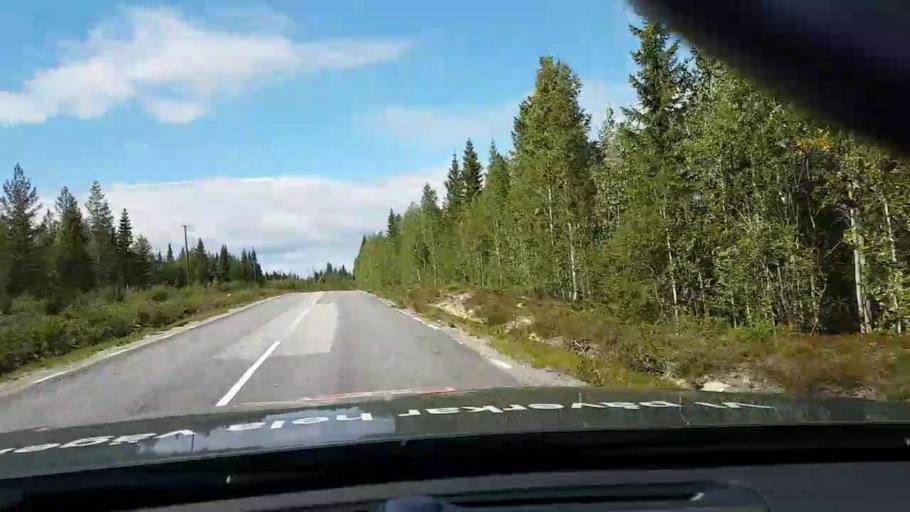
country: SE
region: Vaesterbotten
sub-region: Asele Kommun
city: Asele
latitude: 63.8199
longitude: 17.4904
